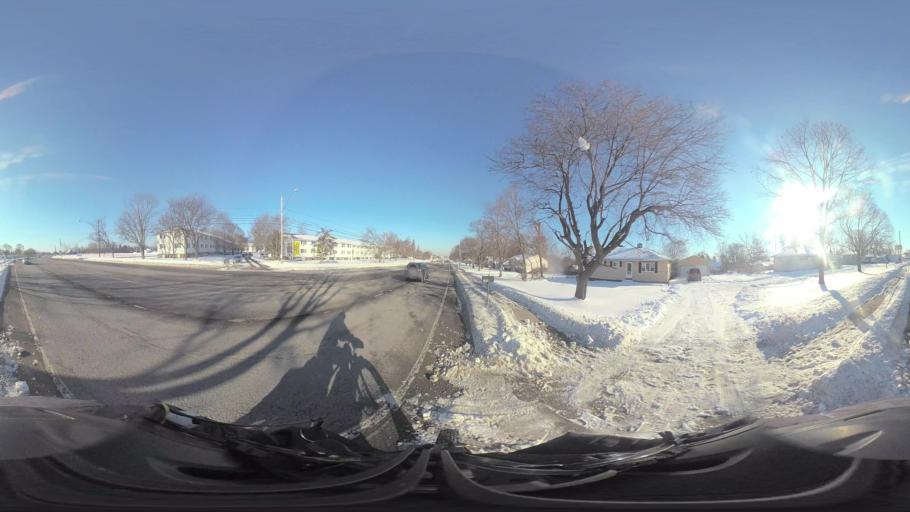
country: US
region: New York
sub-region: Monroe County
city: Rochester
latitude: 43.0797
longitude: -77.6064
